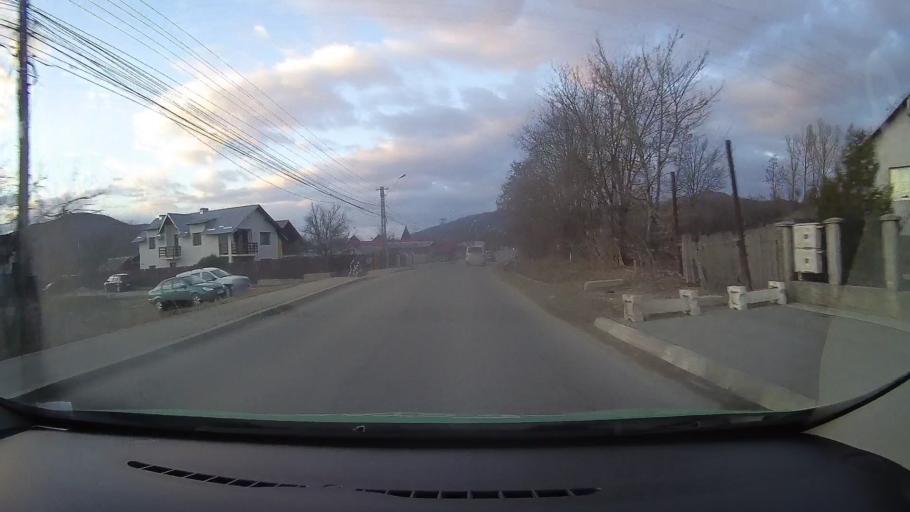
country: RO
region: Dambovita
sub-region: Municipiul Moreni
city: Moreni
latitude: 45.0014
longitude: 25.6470
